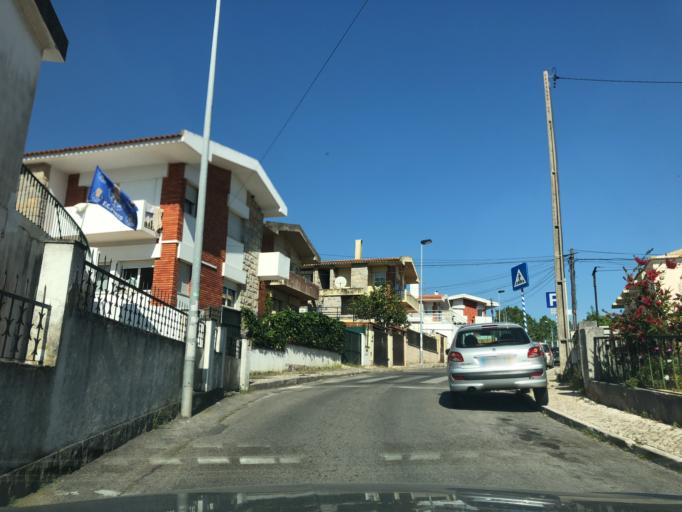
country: PT
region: Lisbon
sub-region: Oeiras
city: Terrugem
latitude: 38.7081
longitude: -9.2771
